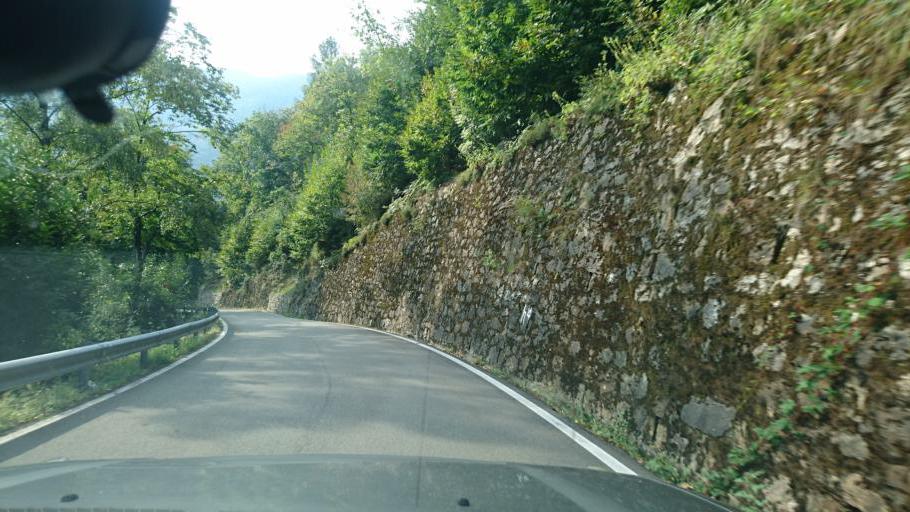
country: IT
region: Lombardy
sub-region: Provincia di Brescia
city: Paisco Loveno
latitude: 46.0889
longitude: 10.3044
